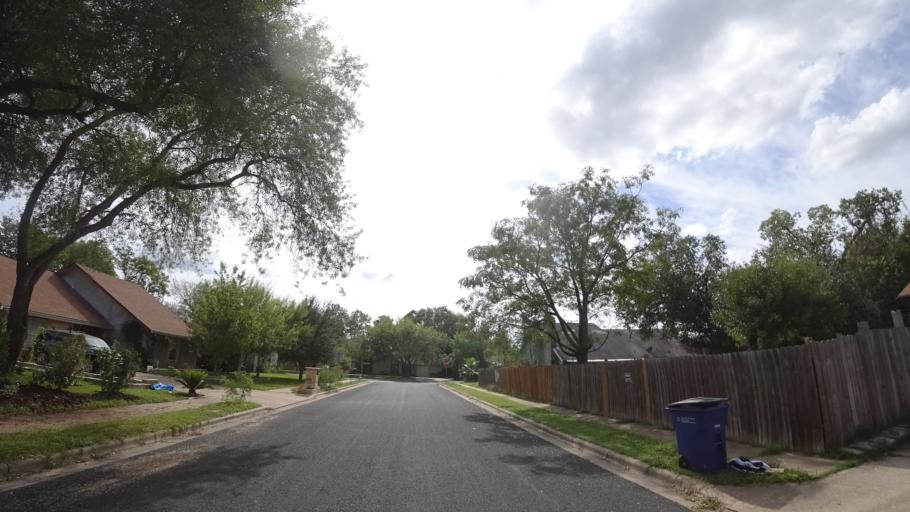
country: US
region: Texas
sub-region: Travis County
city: Austin
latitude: 30.1993
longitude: -97.7416
